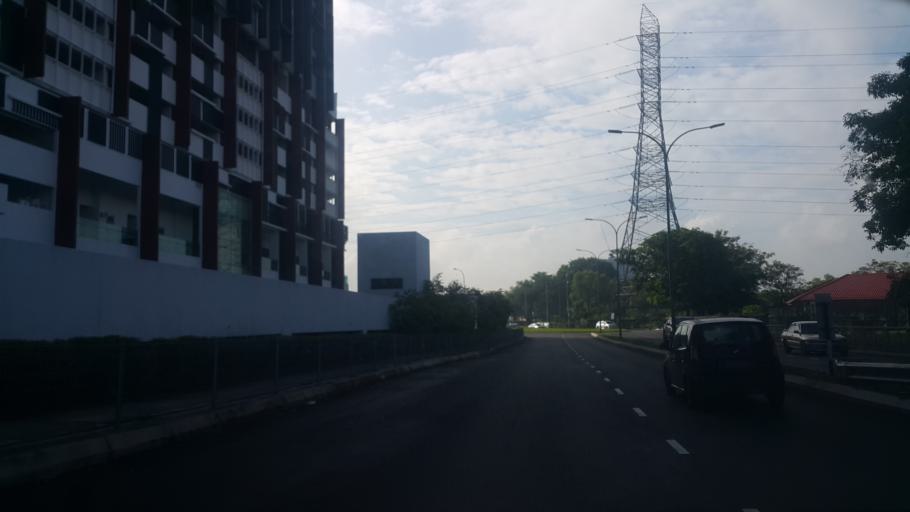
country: MY
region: Selangor
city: Klang
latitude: 2.9930
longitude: 101.4432
